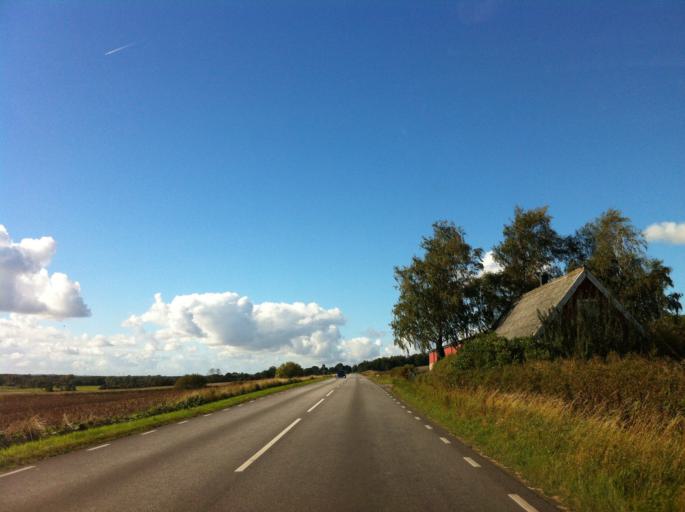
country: SE
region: Skane
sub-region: Hoors Kommun
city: Loberod
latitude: 55.7171
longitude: 13.5259
